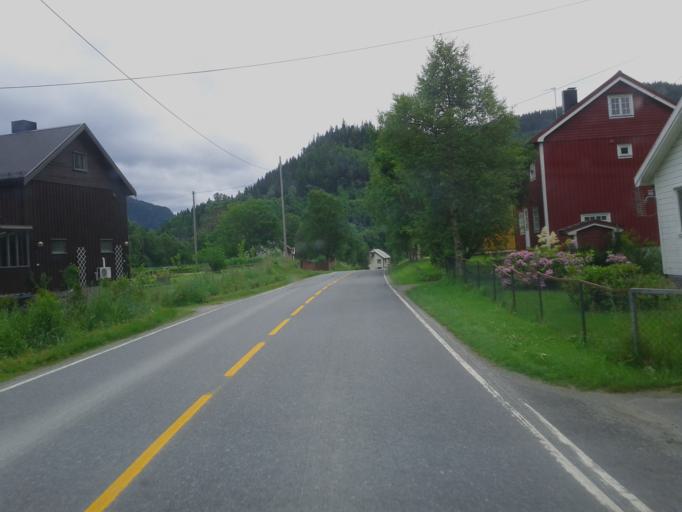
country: NO
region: Sor-Trondelag
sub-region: Midtre Gauldal
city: Storen
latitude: 62.9933
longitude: 10.4895
